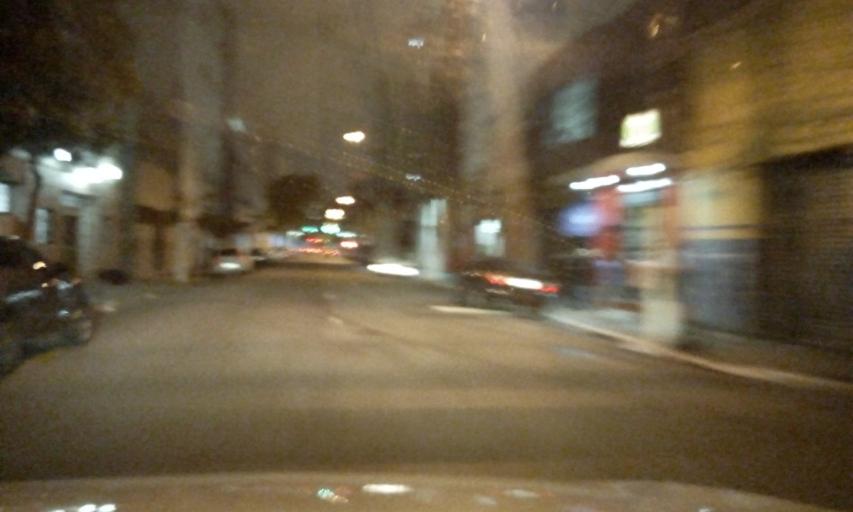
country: BR
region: Sao Paulo
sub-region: Sao Paulo
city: Sao Paulo
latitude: -23.5513
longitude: -46.6195
